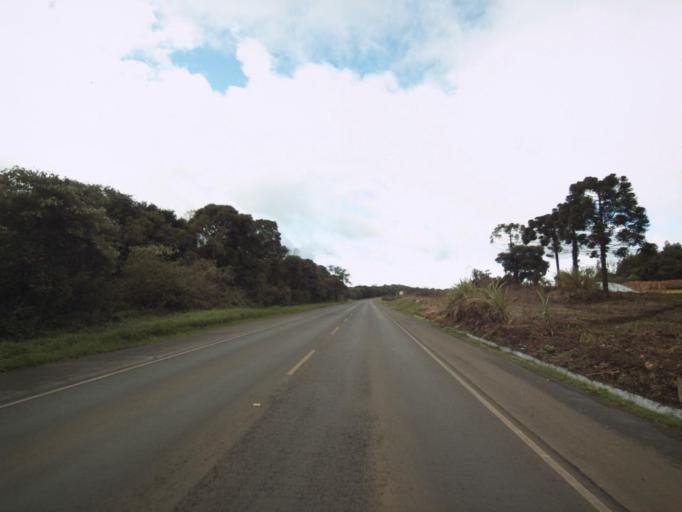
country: BR
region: Santa Catarina
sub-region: Concordia
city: Concordia
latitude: -27.0922
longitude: -51.9047
